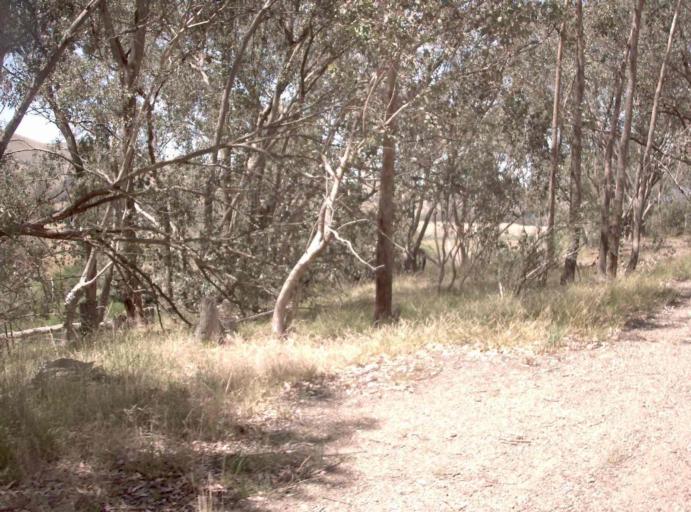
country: AU
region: Victoria
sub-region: East Gippsland
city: Bairnsdale
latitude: -37.2165
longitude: 147.7165
